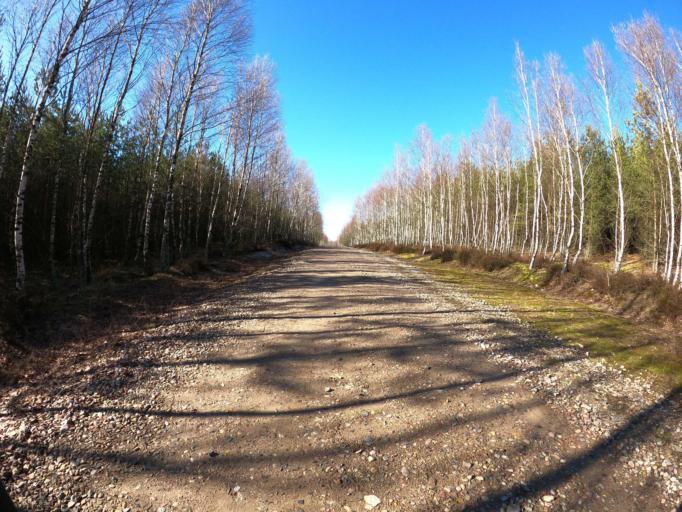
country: PL
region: Greater Poland Voivodeship
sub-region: Powiat zlotowski
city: Sypniewo
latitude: 53.5344
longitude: 16.6048
